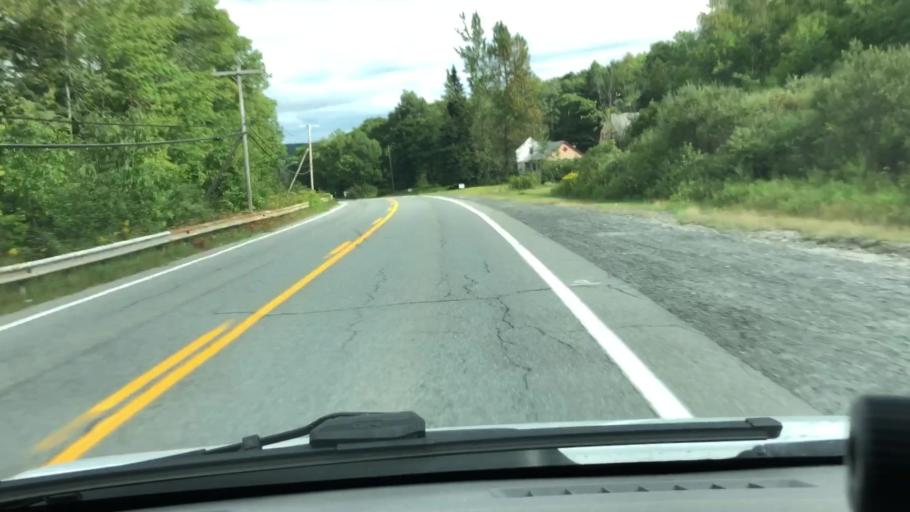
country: US
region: Massachusetts
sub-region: Berkshire County
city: North Adams
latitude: 42.6951
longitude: -73.0593
